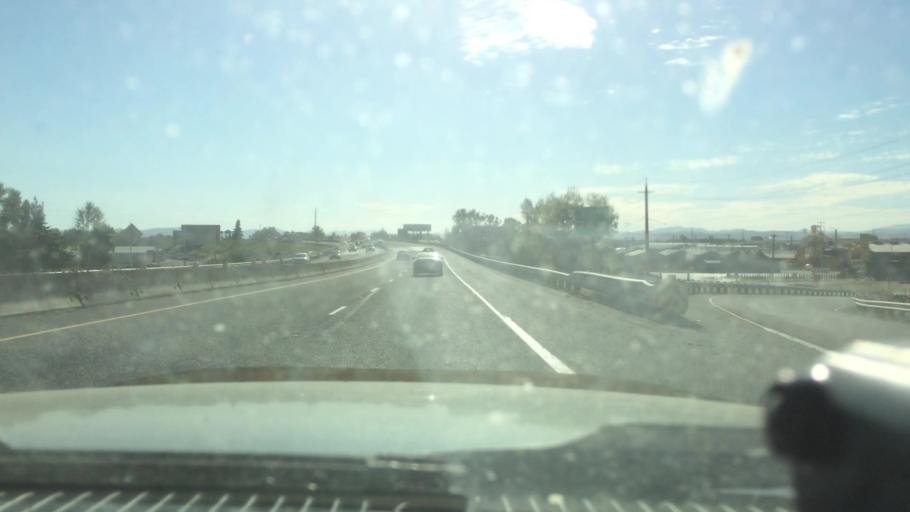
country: US
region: Oregon
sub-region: Lane County
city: Eugene
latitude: 44.0980
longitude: -123.1583
